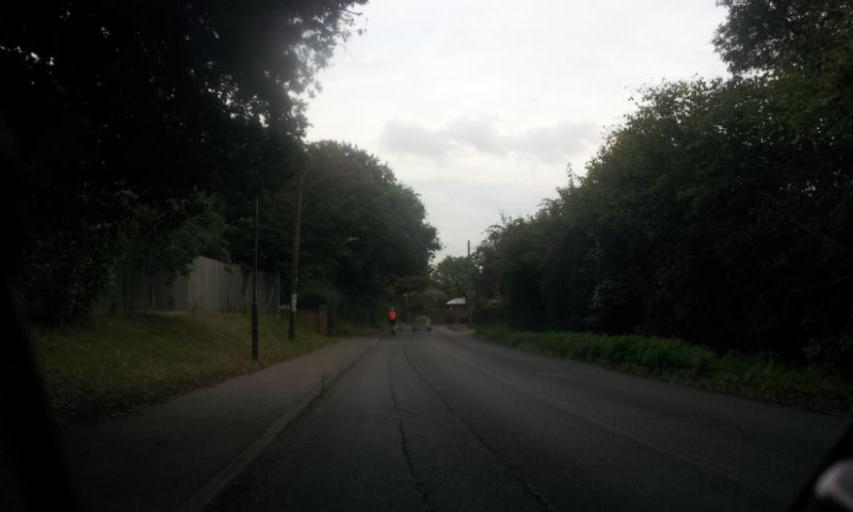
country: GB
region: England
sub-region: Kent
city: Hadlow
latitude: 51.2095
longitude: 0.3503
